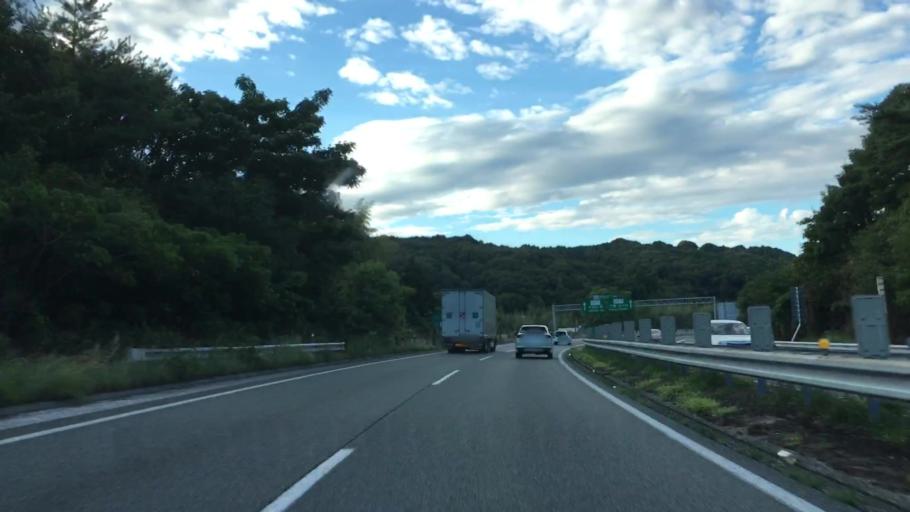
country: JP
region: Yamaguchi
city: Ogori-shimogo
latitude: 34.1633
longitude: 131.3268
